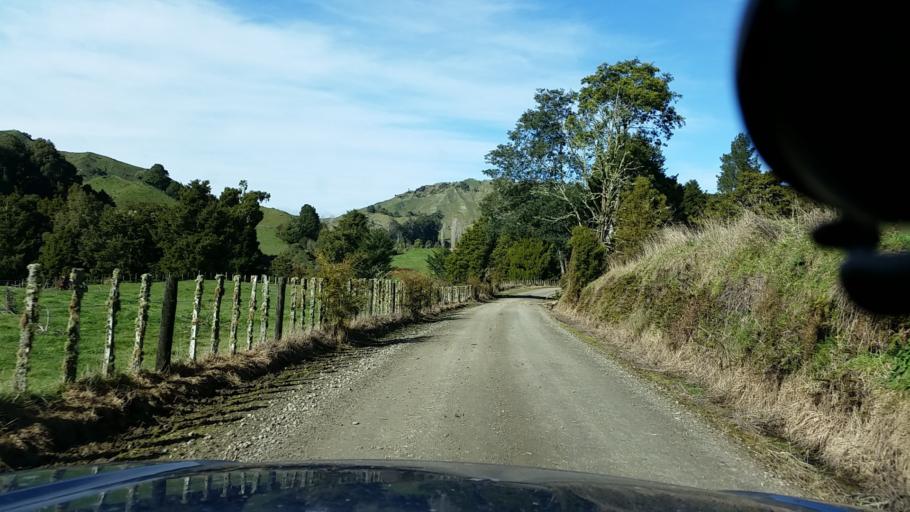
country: NZ
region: Taranaki
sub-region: New Plymouth District
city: Waitara
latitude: -39.0528
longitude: 174.7718
